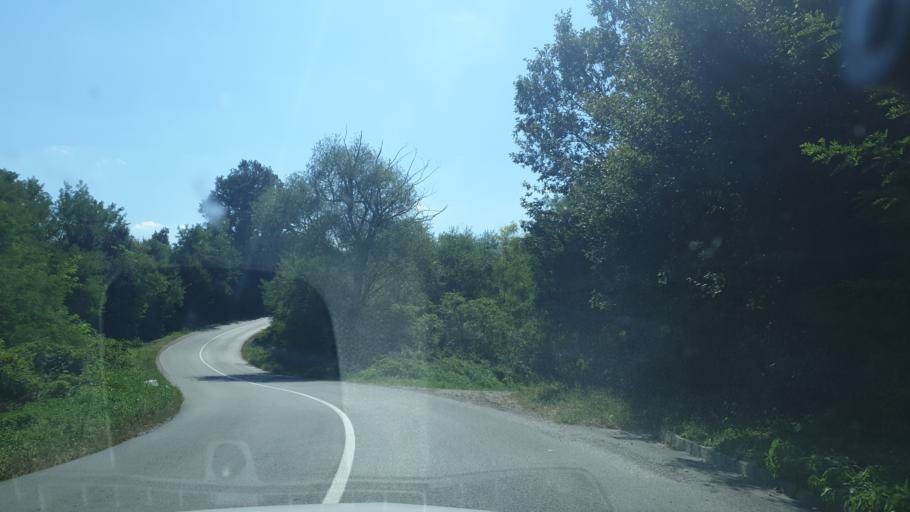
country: RS
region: Central Serbia
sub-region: Kolubarski Okrug
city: Mionica
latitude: 44.1873
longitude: 20.0347
